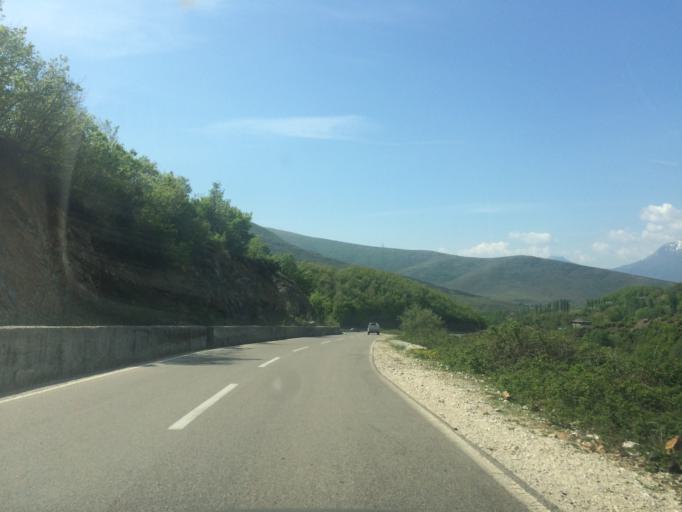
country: AL
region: Kukes
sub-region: Rrethi i Tropojes
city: Bytyc
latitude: 42.3939
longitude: 20.1839
